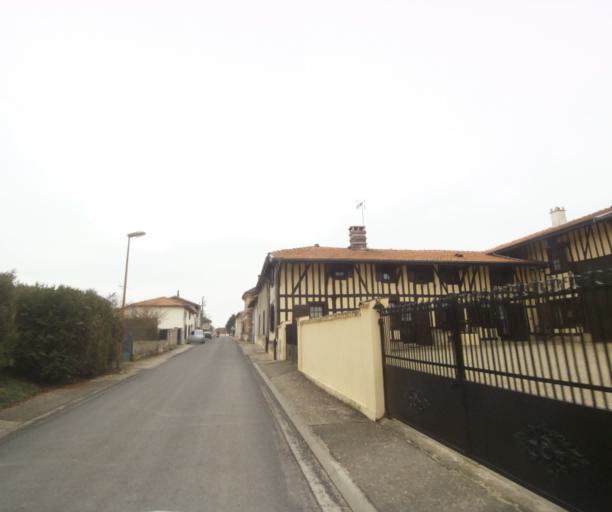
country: FR
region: Champagne-Ardenne
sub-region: Departement de la Haute-Marne
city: Villiers-en-Lieu
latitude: 48.6344
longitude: 4.8381
